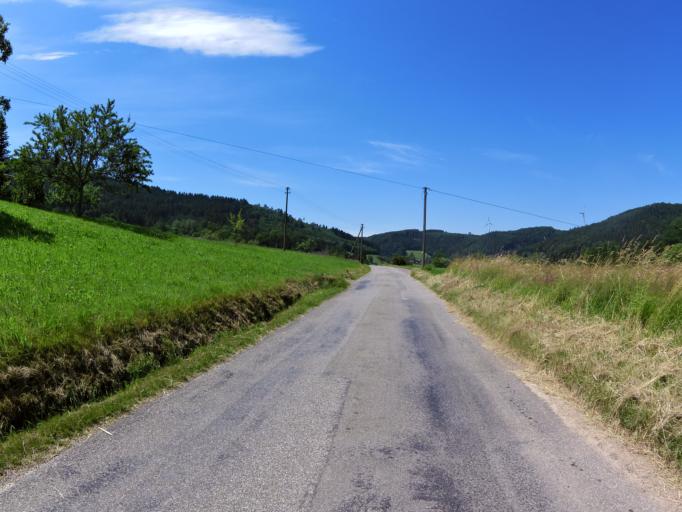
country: DE
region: Baden-Wuerttemberg
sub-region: Freiburg Region
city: Seelbach
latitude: 48.3014
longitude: 7.9349
